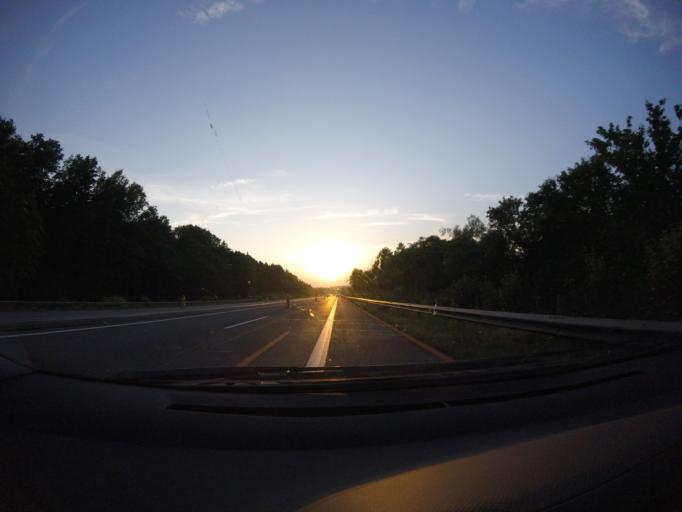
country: AT
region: Styria
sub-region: Politischer Bezirk Weiz
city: Sinabelkirchen
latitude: 47.0944
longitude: 15.8291
